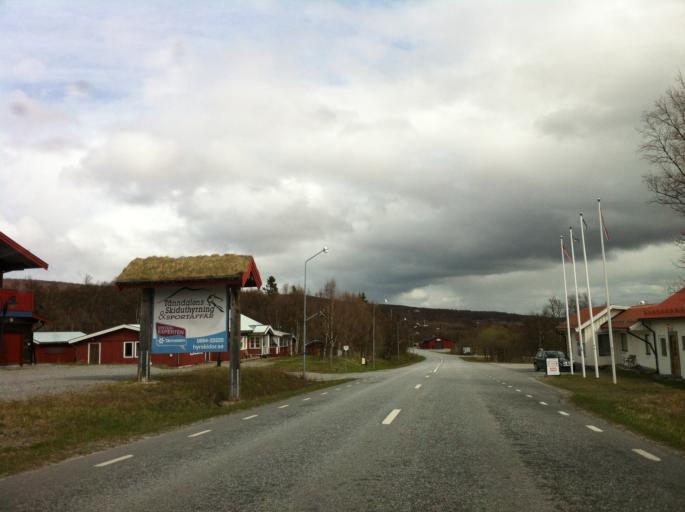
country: NO
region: Sor-Trondelag
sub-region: Tydal
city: Aas
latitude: 62.5506
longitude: 12.2999
